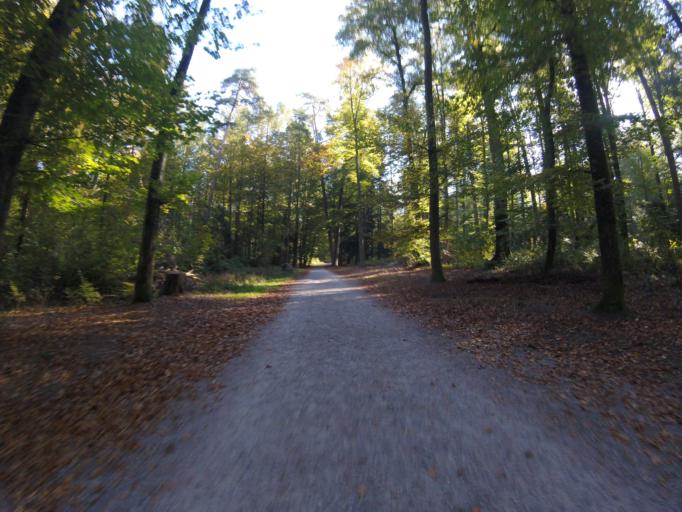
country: CH
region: Bern
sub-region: Bern-Mittelland District
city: Bern
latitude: 46.9376
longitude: 7.4579
